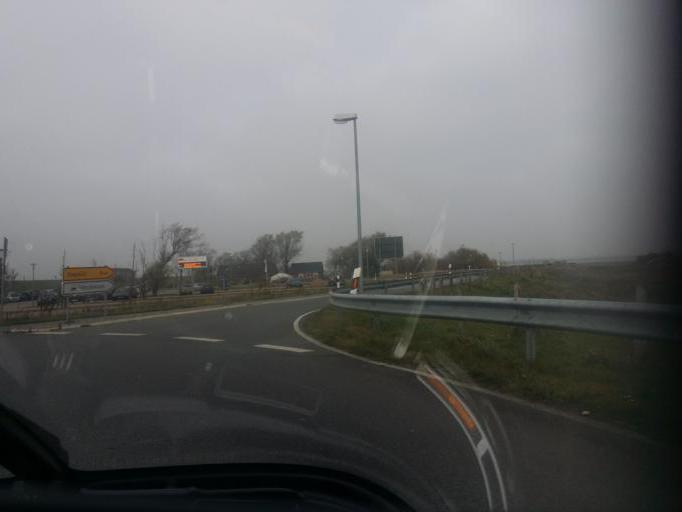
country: DE
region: Schleswig-Holstein
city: Grode
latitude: 54.6805
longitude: 8.7582
